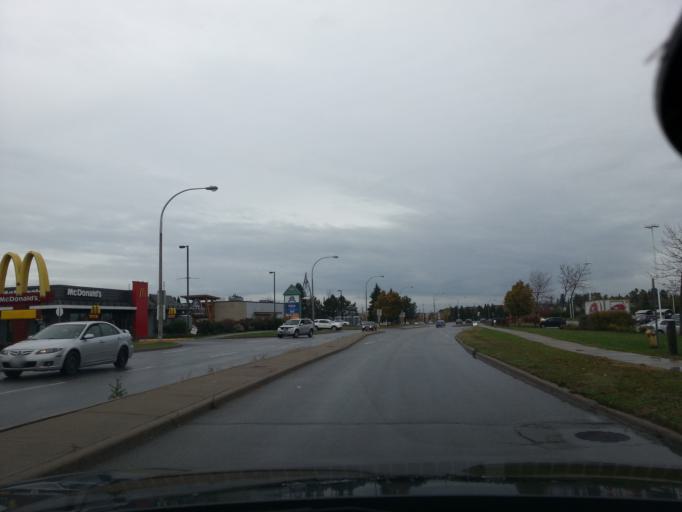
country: CA
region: Ontario
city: Bells Corners
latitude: 45.2679
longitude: -75.9301
